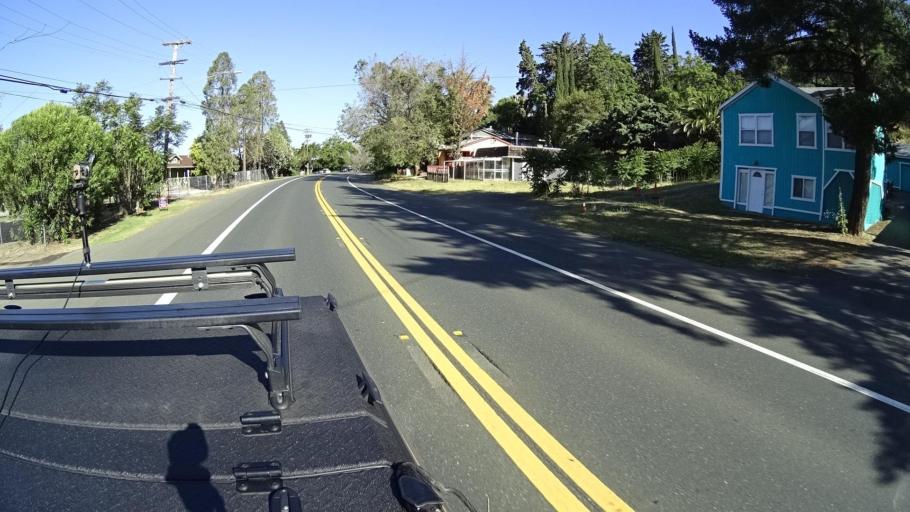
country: US
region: California
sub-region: Lake County
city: Soda Bay
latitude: 39.0267
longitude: -122.7339
